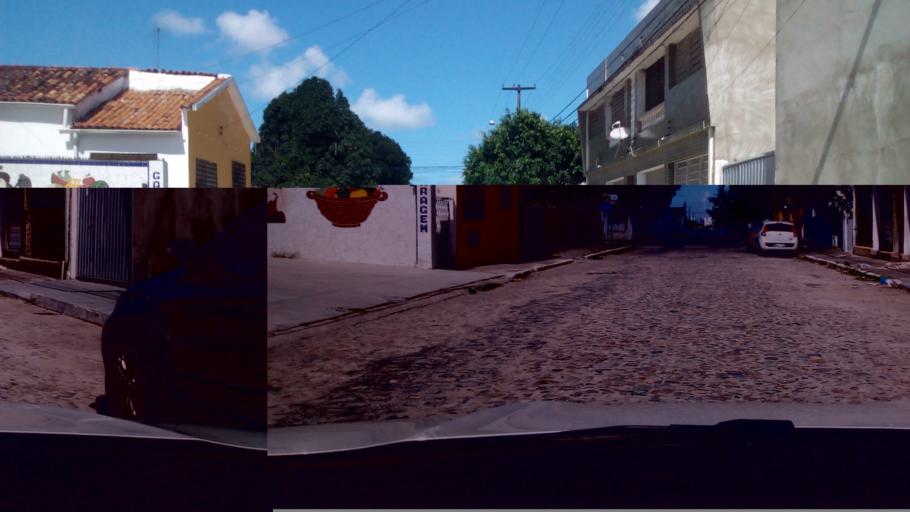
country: BR
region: Paraiba
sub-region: Joao Pessoa
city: Joao Pessoa
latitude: -7.1291
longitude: -34.8832
